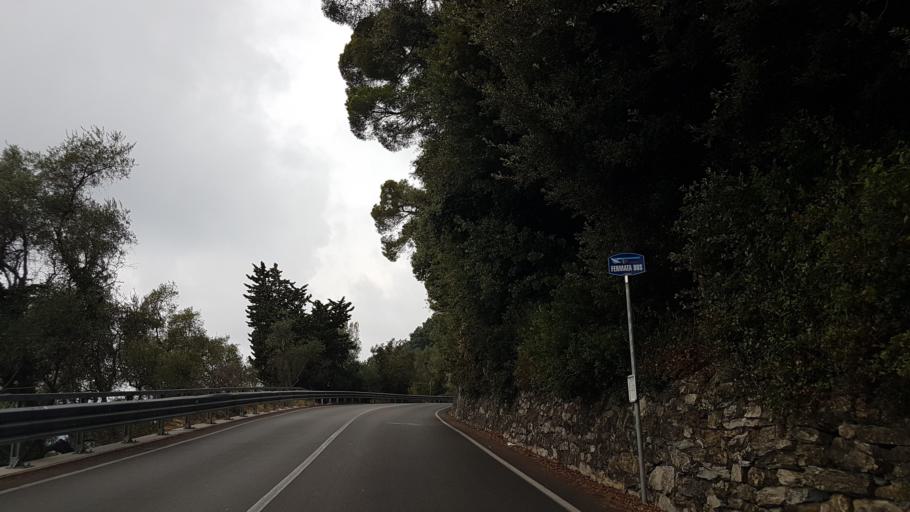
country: IT
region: Liguria
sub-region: Provincia di Genova
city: Chiavari
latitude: 44.3261
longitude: 9.2991
